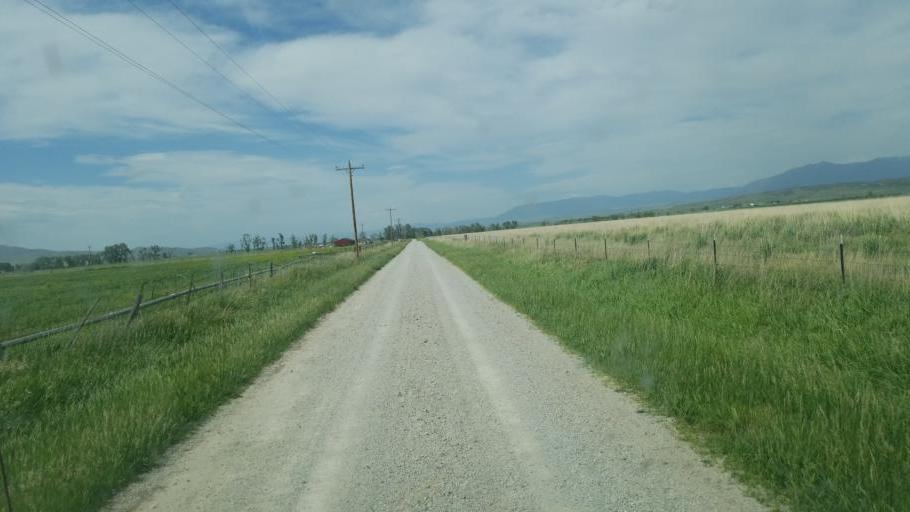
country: US
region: Montana
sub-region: Broadwater County
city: Townsend
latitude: 46.1751
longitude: -111.4720
